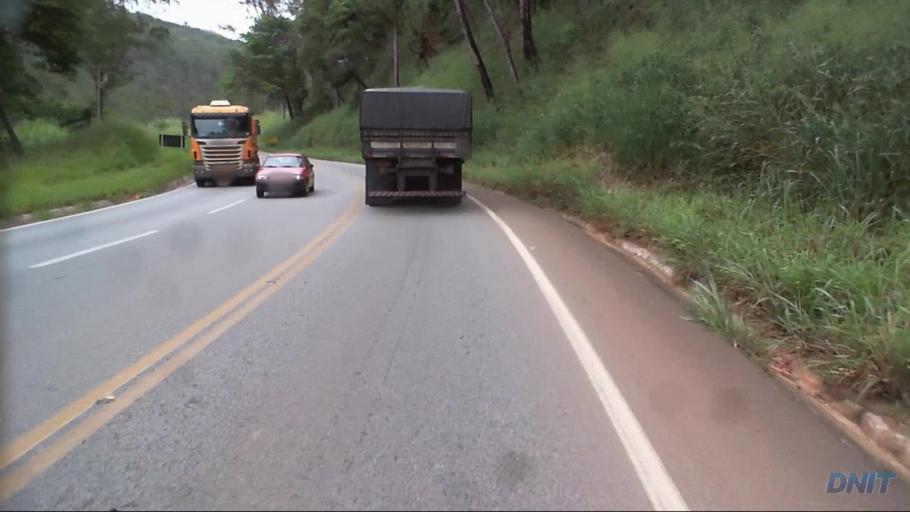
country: BR
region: Minas Gerais
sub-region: Nova Era
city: Nova Era
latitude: -19.8215
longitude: -43.0753
